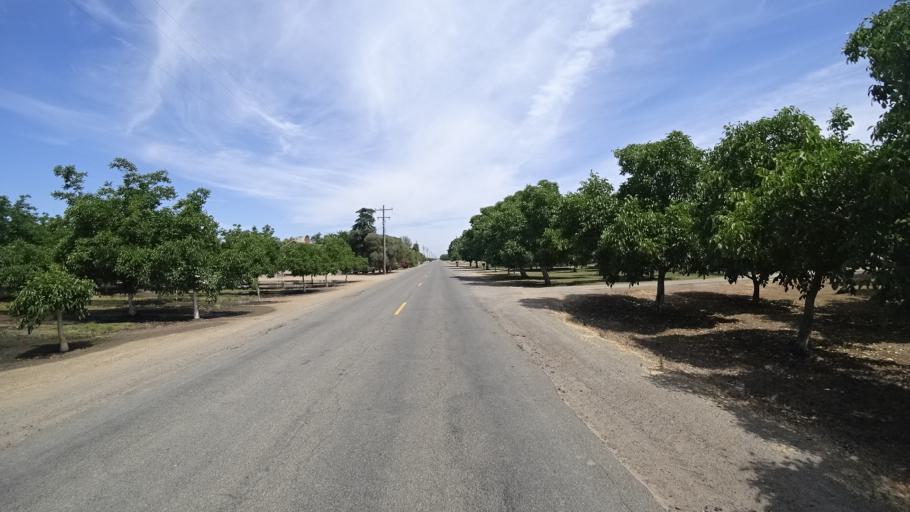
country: US
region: California
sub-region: Kings County
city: Lucerne
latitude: 36.3620
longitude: -119.6910
